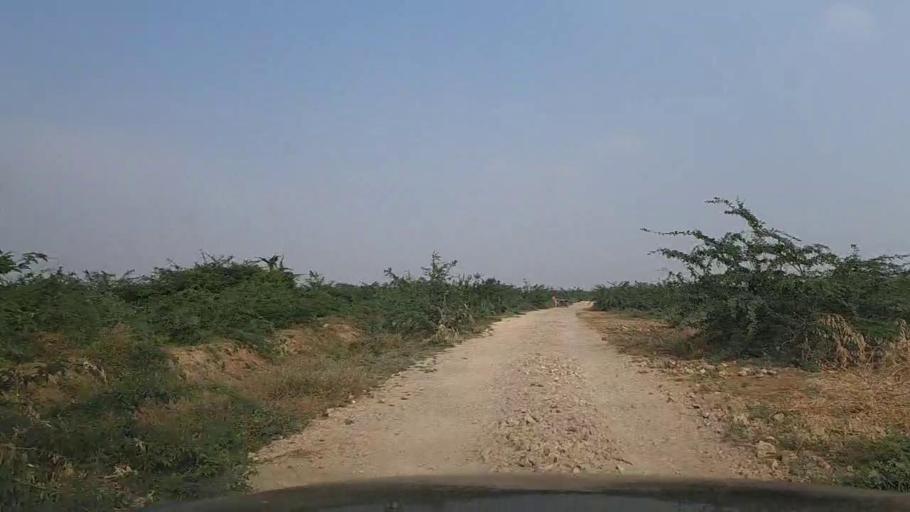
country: PK
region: Sindh
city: Thatta
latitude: 24.8641
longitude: 67.8011
